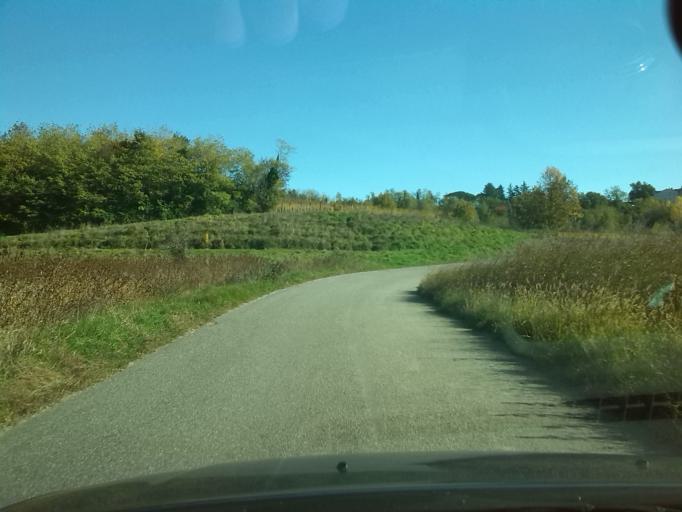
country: SI
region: Brda
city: Dobrovo
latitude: 45.9838
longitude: 13.4947
